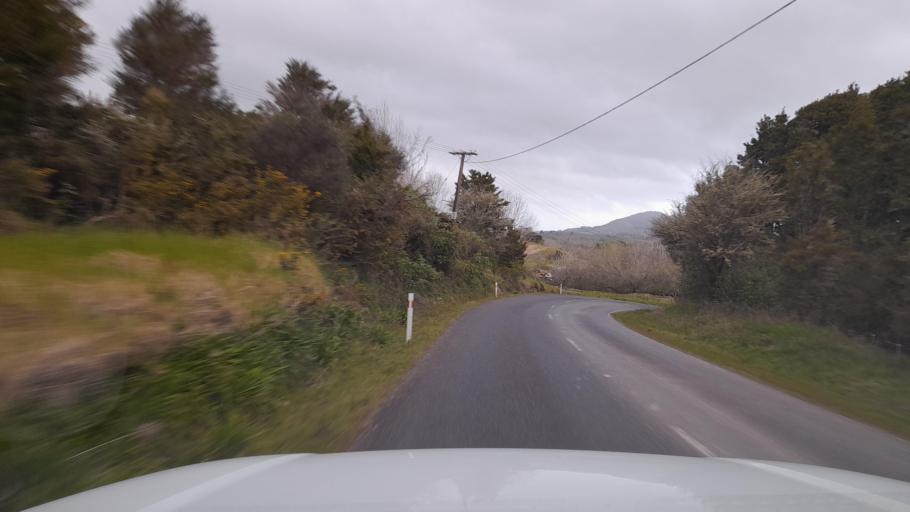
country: NZ
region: Northland
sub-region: Whangarei
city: Maungatapere
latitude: -35.6341
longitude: 174.2035
